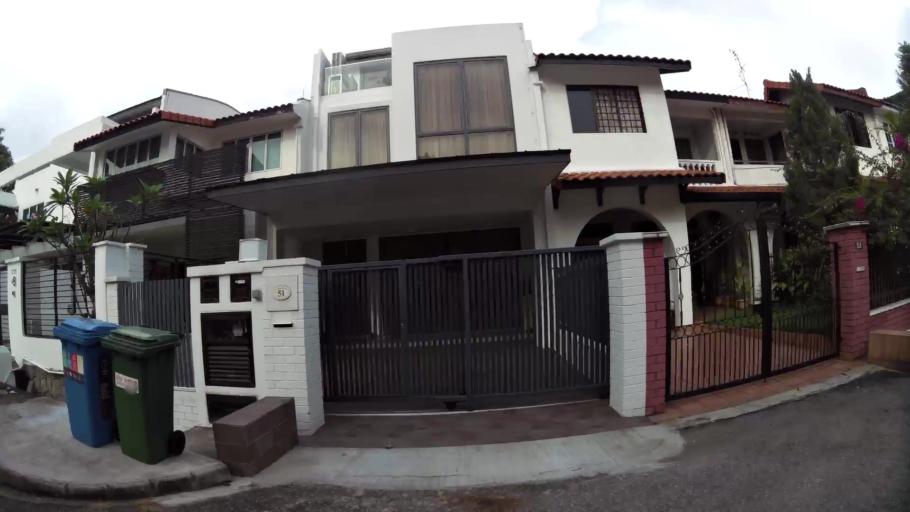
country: SG
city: Singapore
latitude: 1.3511
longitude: 103.8438
